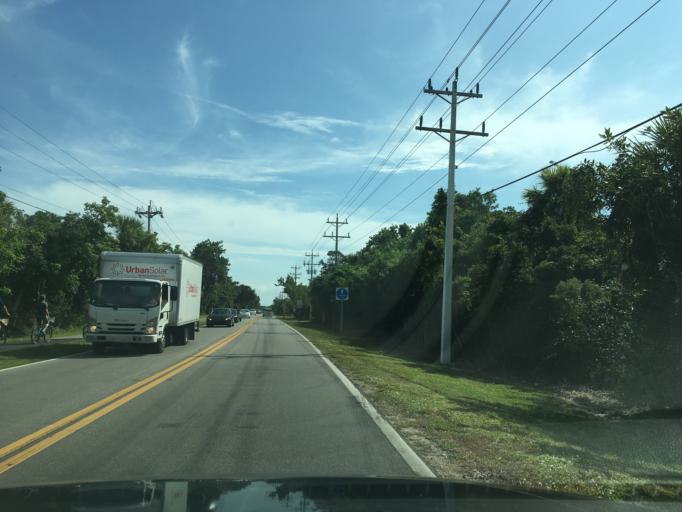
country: US
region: Florida
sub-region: Lee County
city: Saint James City
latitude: 26.4431
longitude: -82.1097
